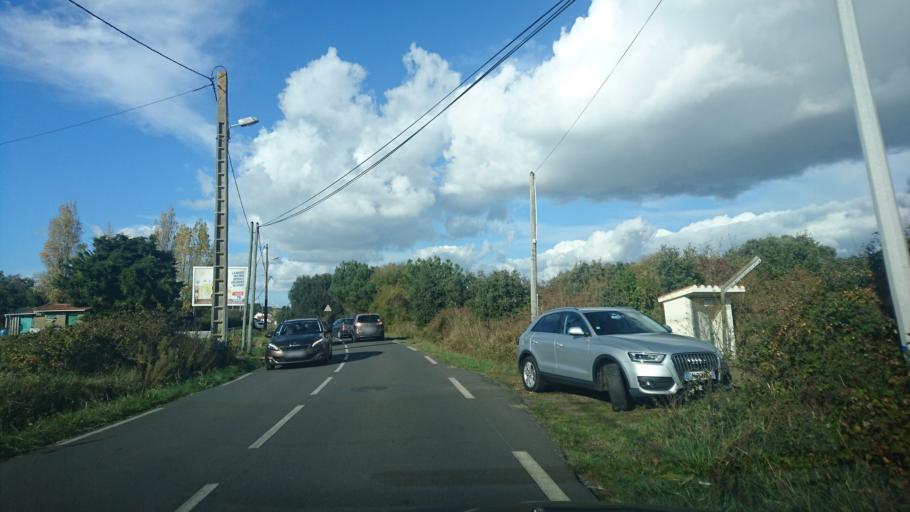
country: FR
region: Pays de la Loire
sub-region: Departement de la Vendee
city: Les Sables-d'Olonne
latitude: 46.5130
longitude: -1.8041
